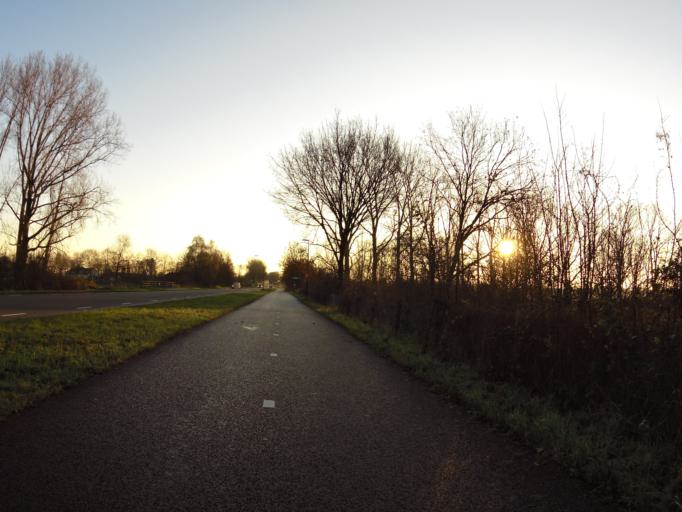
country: NL
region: North Brabant
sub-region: Gemeente Vught
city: Vught
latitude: 51.6494
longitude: 5.3182
